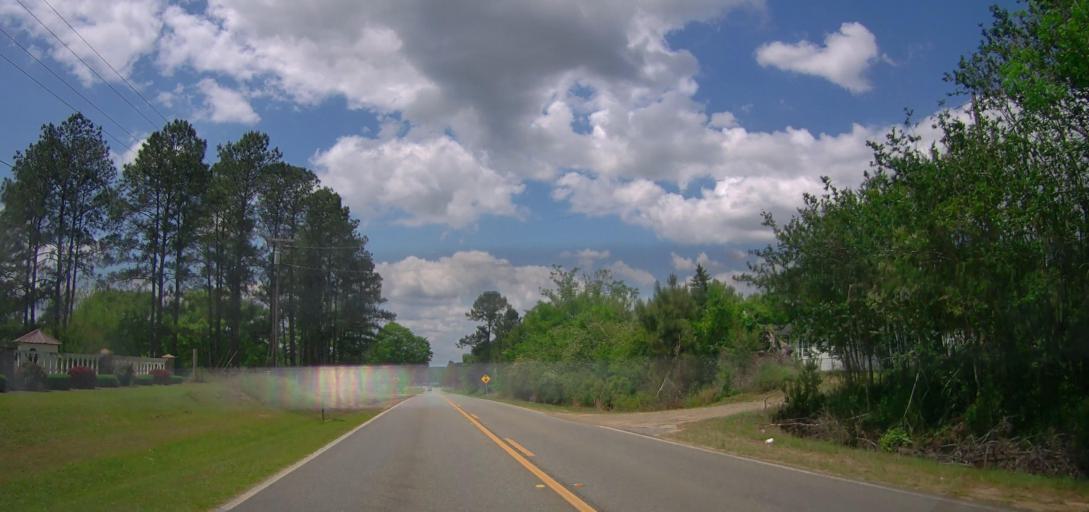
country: US
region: Georgia
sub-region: Laurens County
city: East Dublin
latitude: 32.5206
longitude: -82.8015
